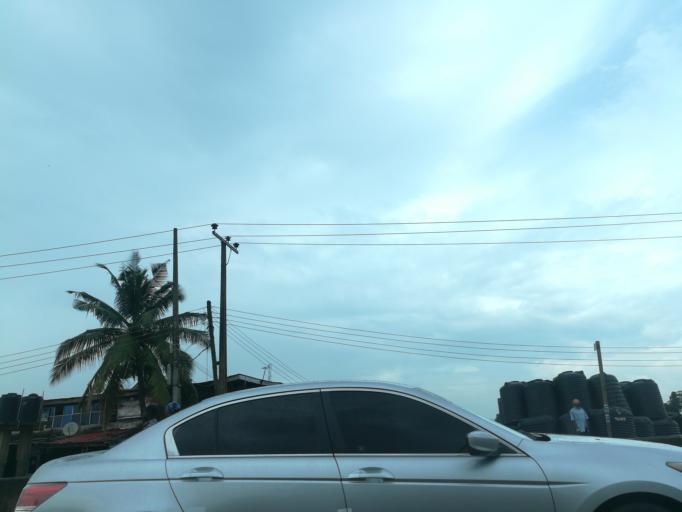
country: NG
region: Lagos
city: Ikorodu
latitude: 6.6294
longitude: 3.5074
